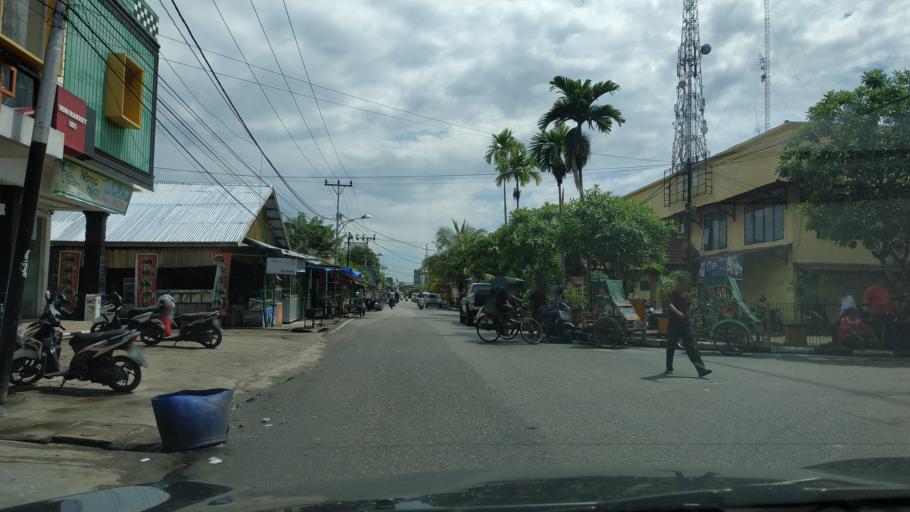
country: ID
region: Riau
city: Tembilahan
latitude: -0.3249
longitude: 103.1571
